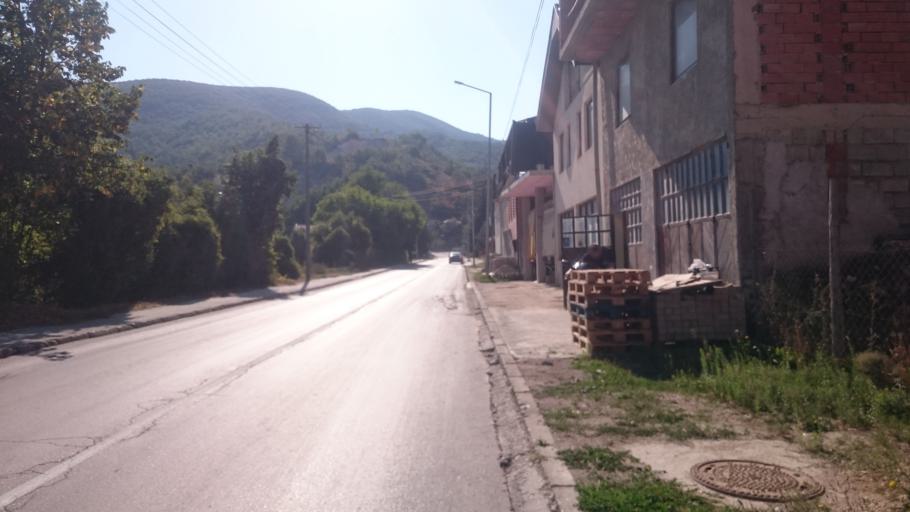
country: MK
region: Makedonski Brod
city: Makedonski Brod
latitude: 41.5071
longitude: 21.2226
